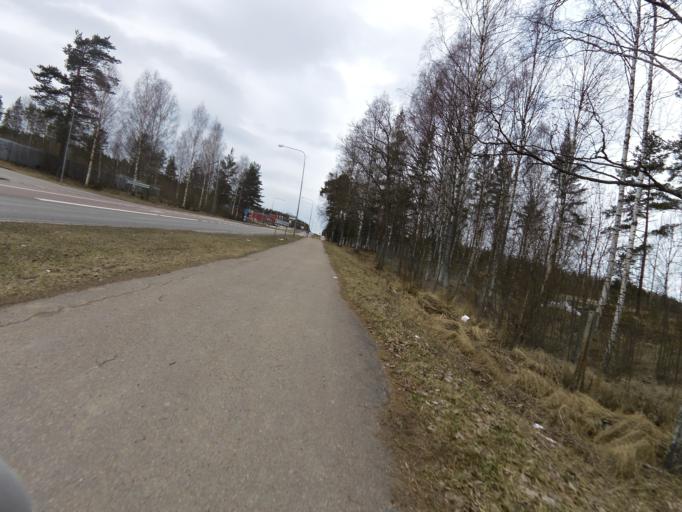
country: SE
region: Gaevleborg
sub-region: Hofors Kommun
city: Hofors
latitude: 60.5417
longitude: 16.2710
